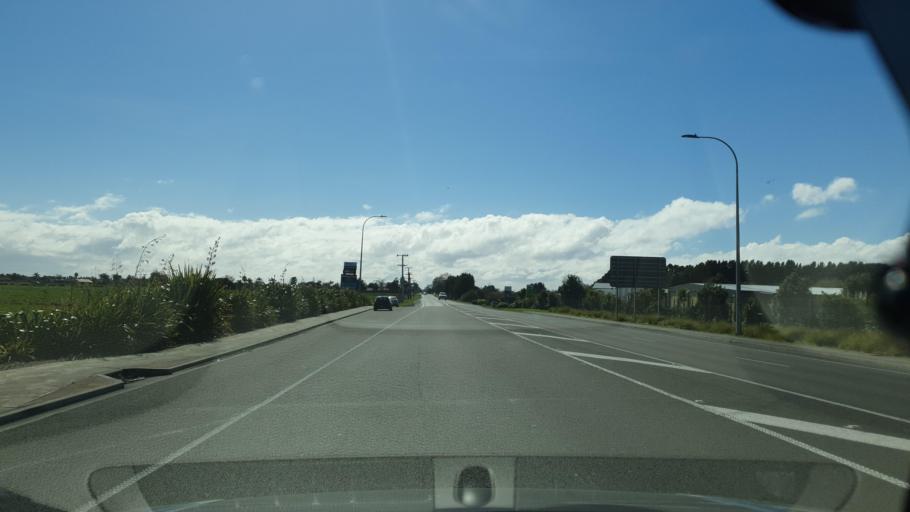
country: NZ
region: Bay of Plenty
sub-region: Tauranga City
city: Tauranga
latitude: -37.7134
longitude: 176.2848
